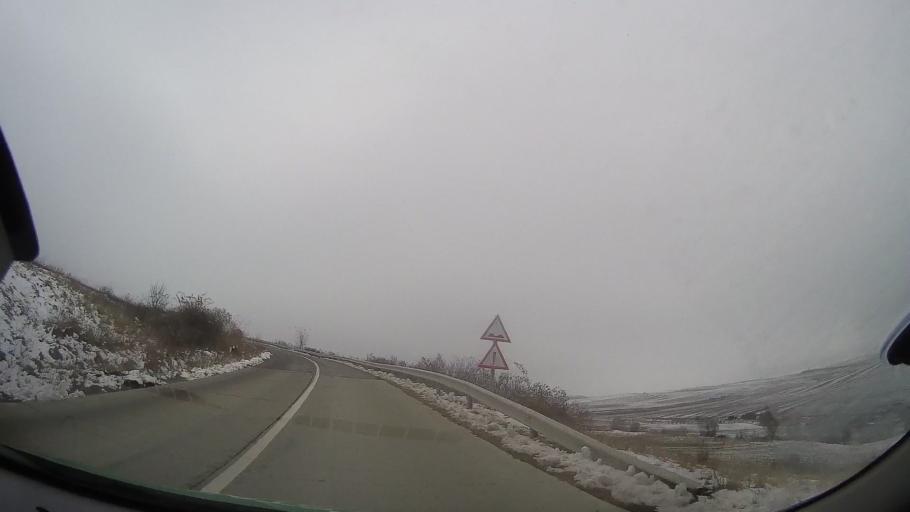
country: RO
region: Vaslui
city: Coroiesti
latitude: 46.2152
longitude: 27.4724
